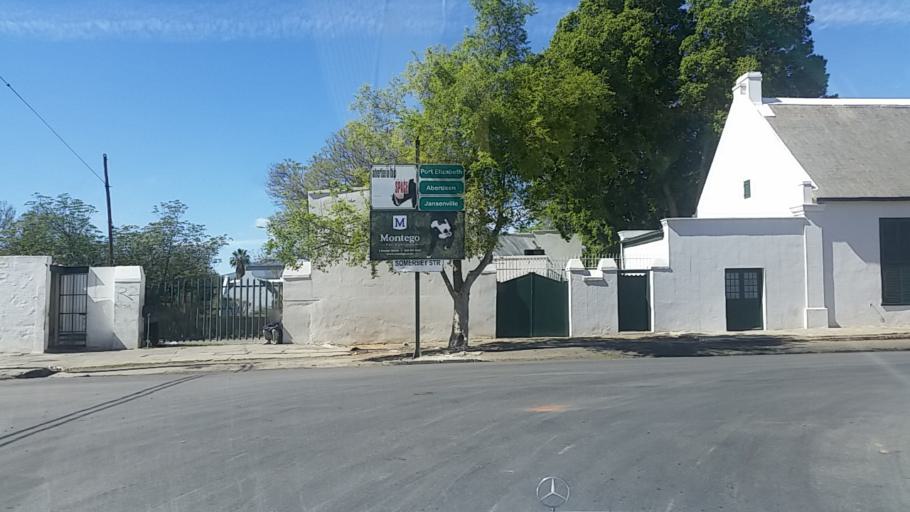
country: ZA
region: Eastern Cape
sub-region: Cacadu District Municipality
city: Graaff-Reinet
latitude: -32.2500
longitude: 24.5386
